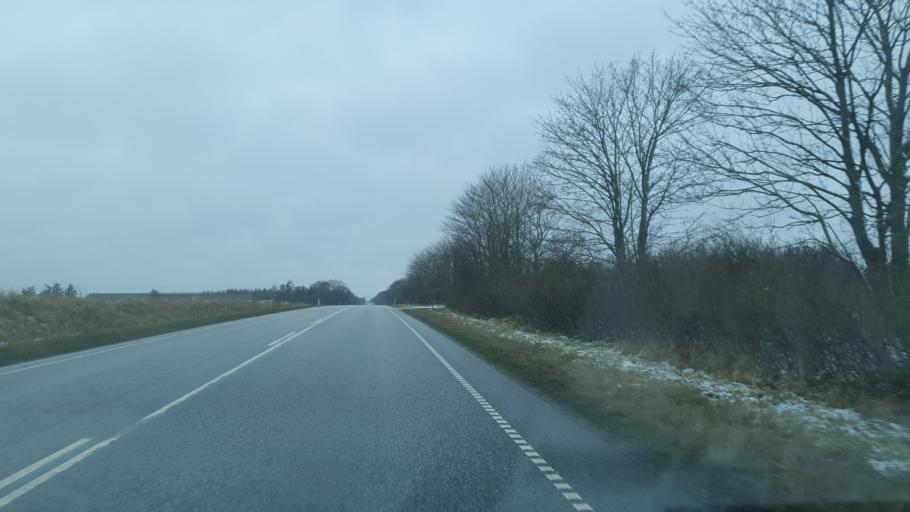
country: DK
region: North Denmark
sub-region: Jammerbugt Kommune
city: Fjerritslev
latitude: 57.0885
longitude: 9.3659
